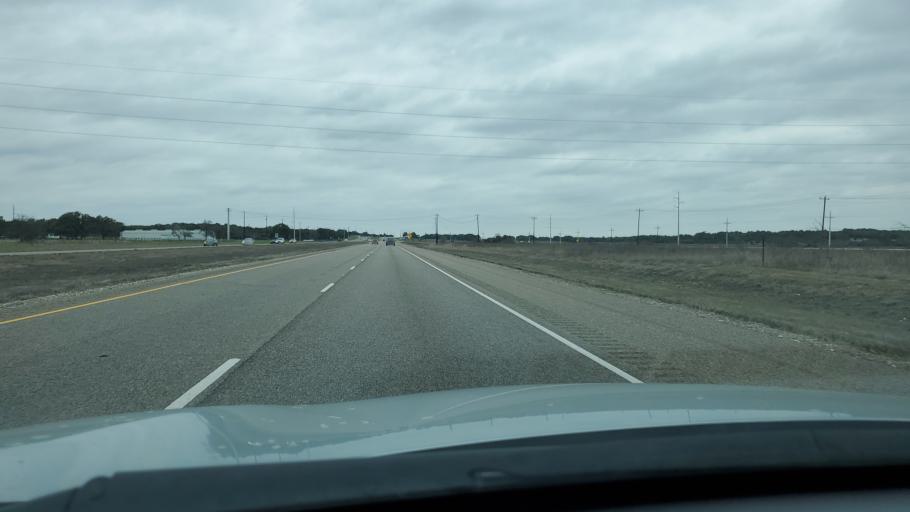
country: US
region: Texas
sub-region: Williamson County
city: Florence
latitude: 30.7837
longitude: -97.7627
